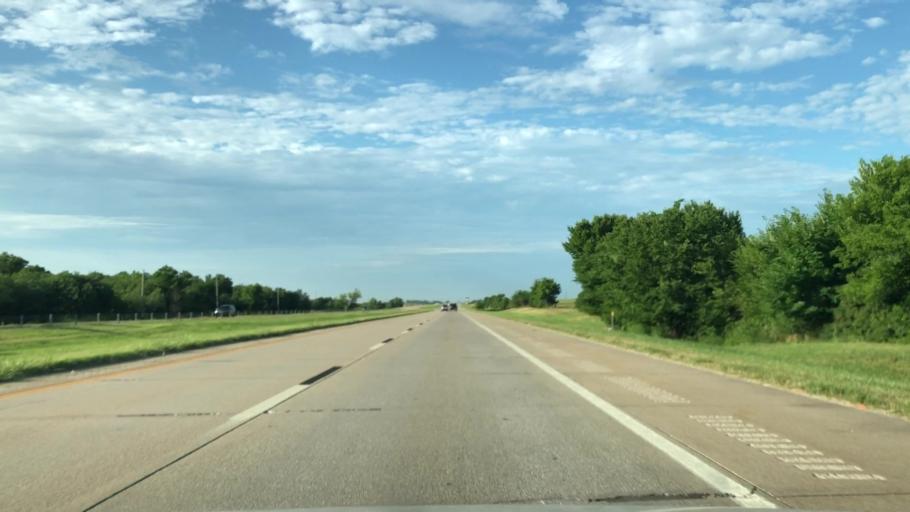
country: US
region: Oklahoma
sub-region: Osage County
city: Skiatook
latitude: 36.3981
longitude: -95.9206
